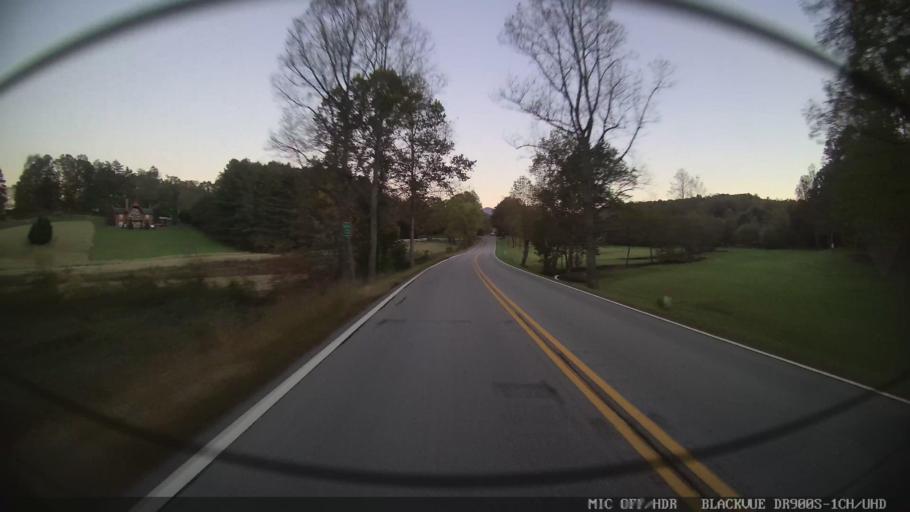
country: US
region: North Carolina
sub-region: Clay County
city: Hayesville
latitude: 34.9673
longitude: -83.8755
